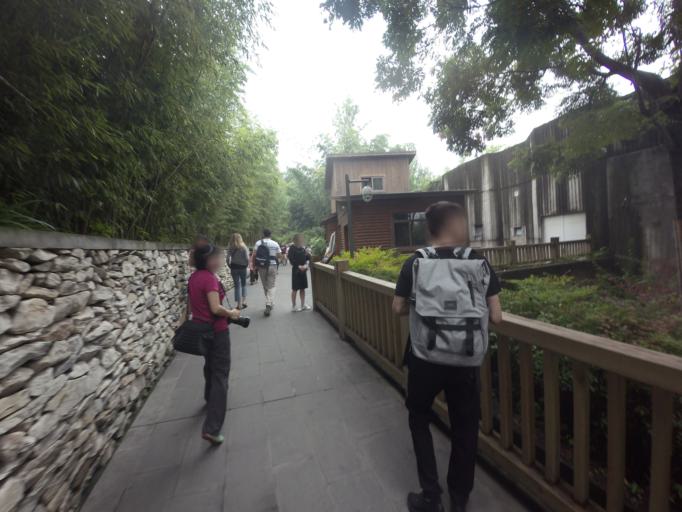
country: CN
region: Sichuan
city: Xindu
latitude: 30.7418
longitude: 104.1376
